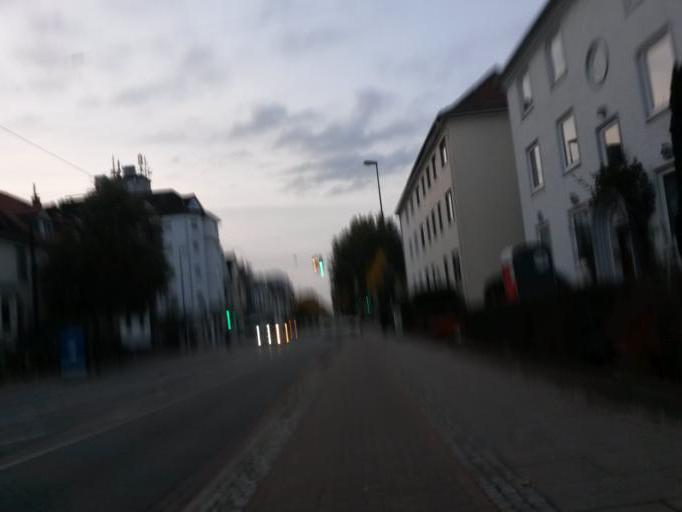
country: DE
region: Bremen
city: Bremen
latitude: 53.0679
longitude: 8.8499
